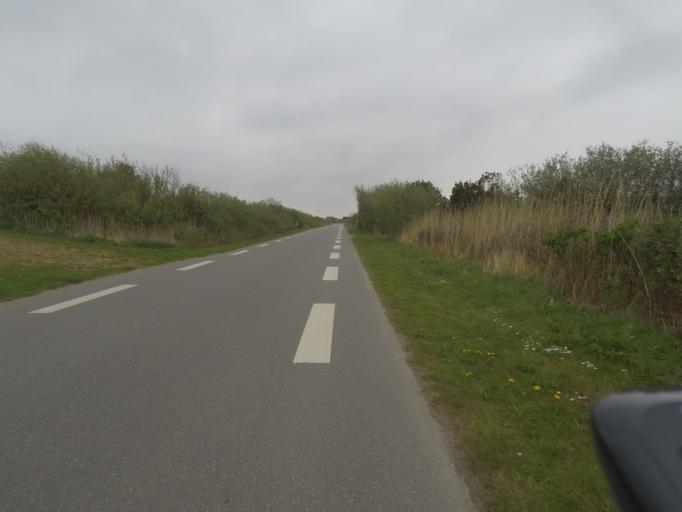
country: DE
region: Schleswig-Holstein
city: List
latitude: 55.1358
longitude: 8.4928
